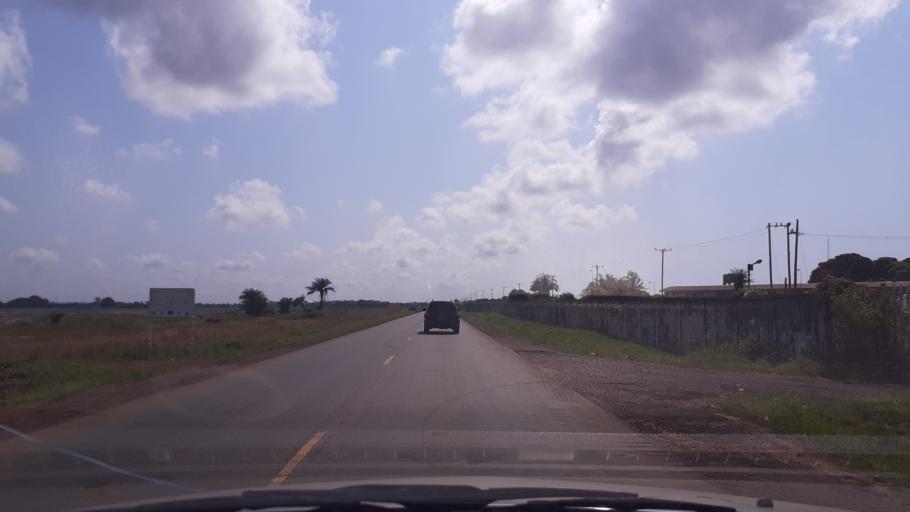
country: LR
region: Montserrado
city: Monrovia
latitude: 6.2153
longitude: -10.5807
